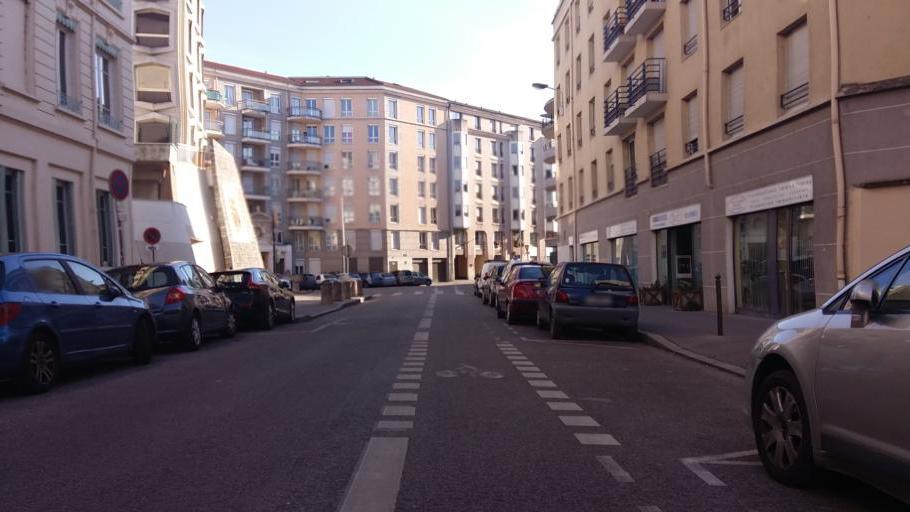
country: FR
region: Rhone-Alpes
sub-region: Departement du Rhone
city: Lyon
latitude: 45.7518
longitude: 4.8506
